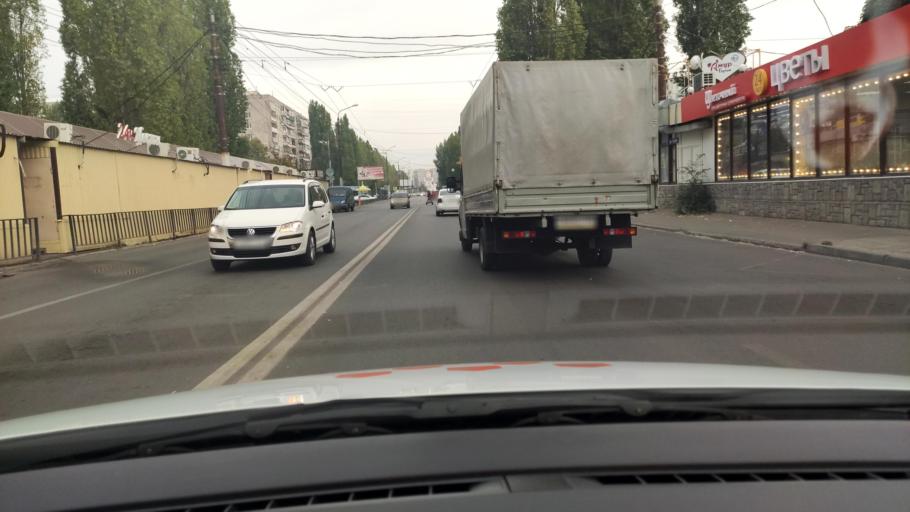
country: RU
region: Voronezj
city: Voronezh
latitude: 51.7068
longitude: 39.1742
